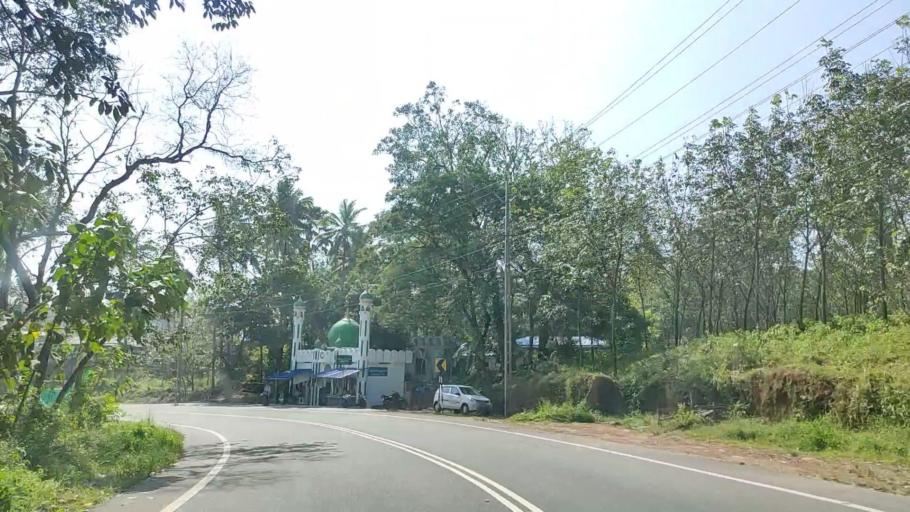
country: IN
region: Kerala
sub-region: Kollam
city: Punalur
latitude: 8.9190
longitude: 77.0384
